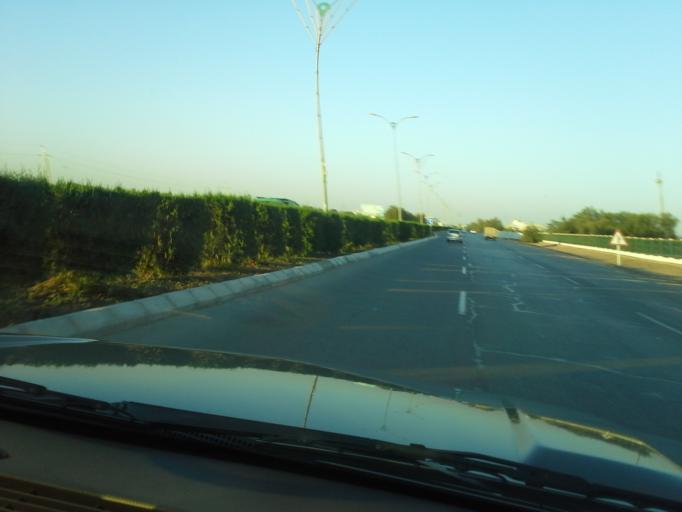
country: TM
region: Dasoguz
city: Dasoguz
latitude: 41.8079
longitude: 59.9075
